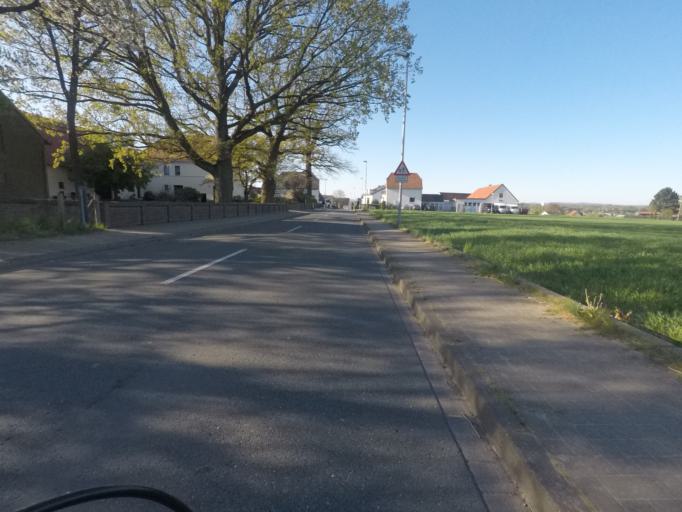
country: DE
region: North Rhine-Westphalia
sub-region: Regierungsbezirk Detmold
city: Hiddenhausen
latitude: 52.1297
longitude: 8.6159
